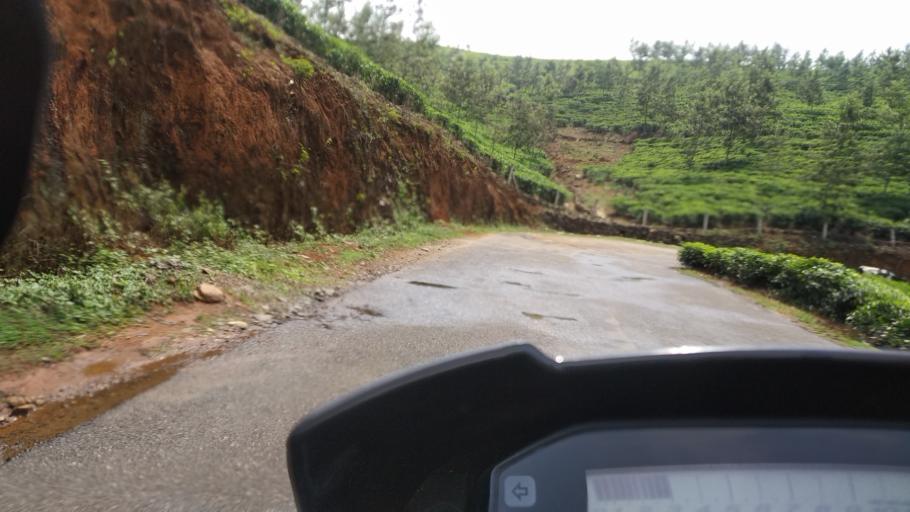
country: IN
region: Kerala
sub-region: Kottayam
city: Erattupetta
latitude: 9.6253
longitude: 76.9738
